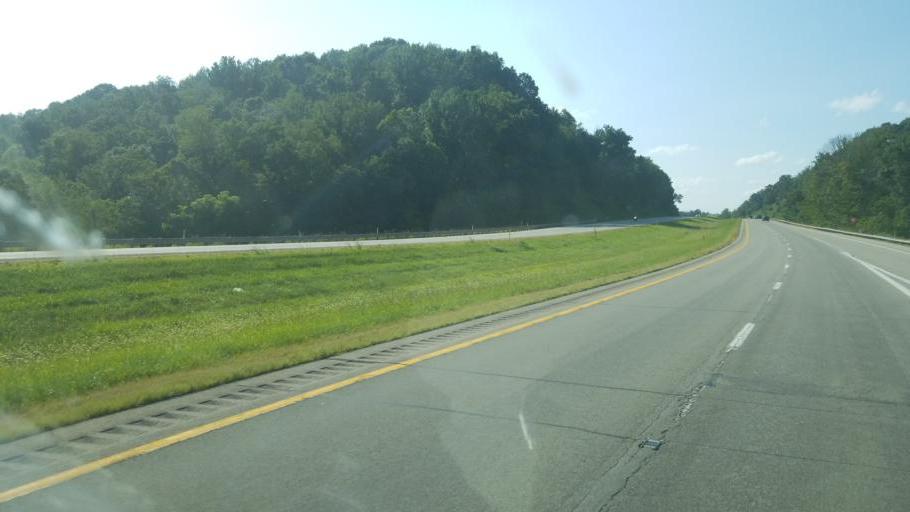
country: US
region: Pennsylvania
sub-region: Greene County
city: Morrisville
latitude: 39.7987
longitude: -80.0789
